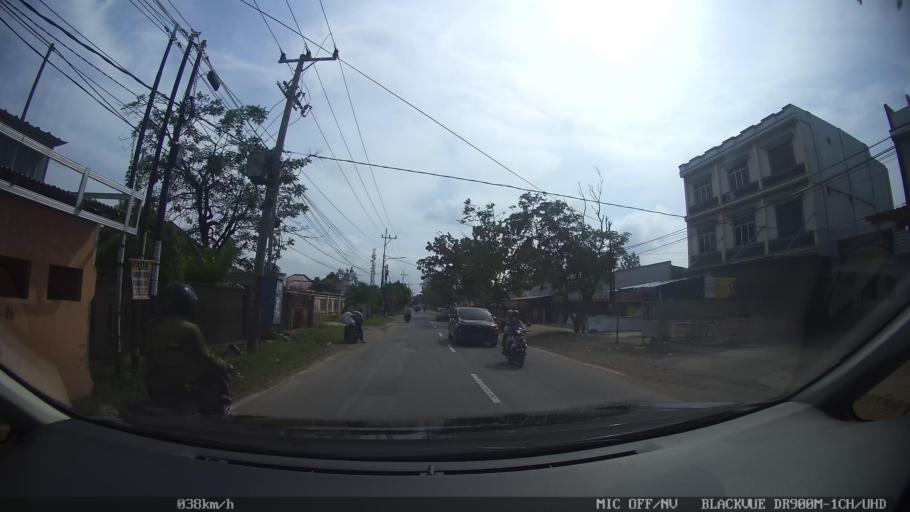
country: ID
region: Lampung
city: Kedaton
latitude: -5.3829
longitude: 105.2972
